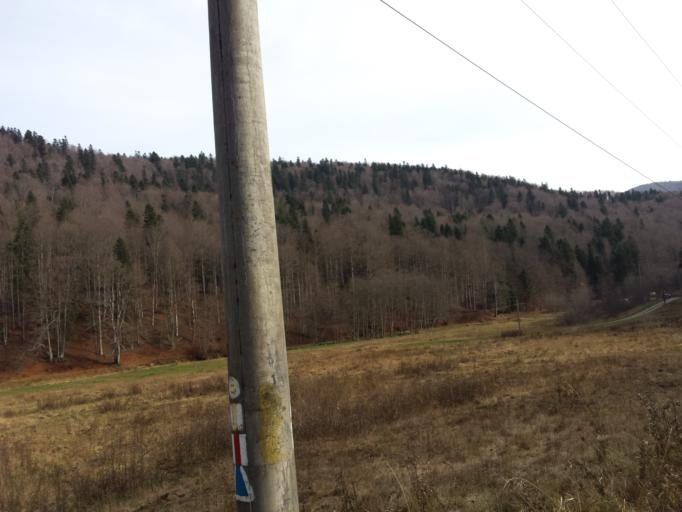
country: RO
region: Prahova
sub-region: Oras Azuga
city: Azuga
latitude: 45.4308
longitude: 25.5316
